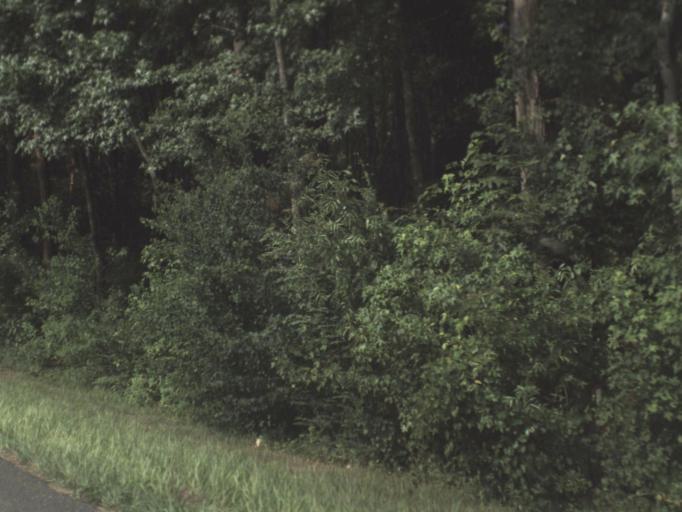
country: US
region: Florida
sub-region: Madison County
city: Madison
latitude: 30.4604
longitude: -83.6319
